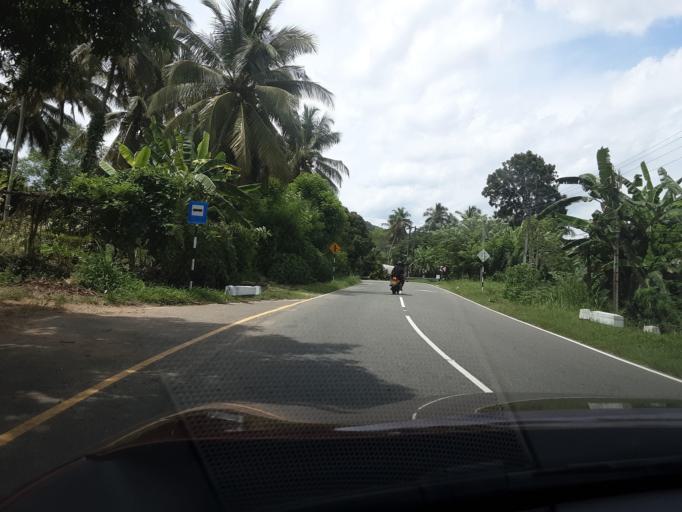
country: LK
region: Uva
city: Monaragala
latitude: 6.8972
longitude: 81.2789
